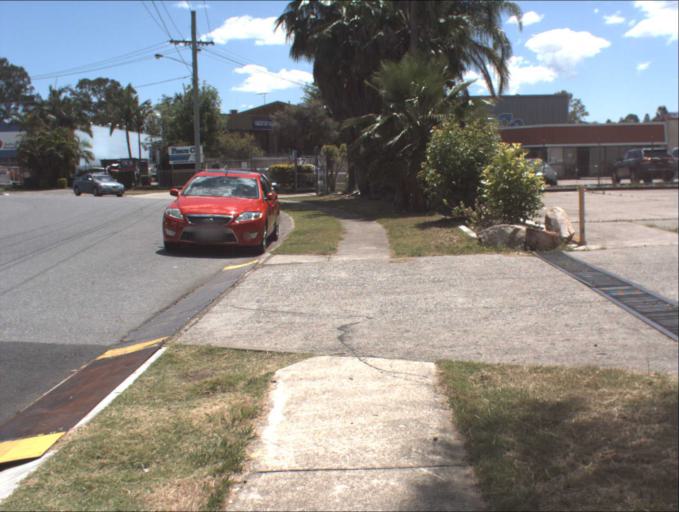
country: AU
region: Queensland
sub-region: Logan
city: Rochedale South
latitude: -27.6073
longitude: 153.1148
